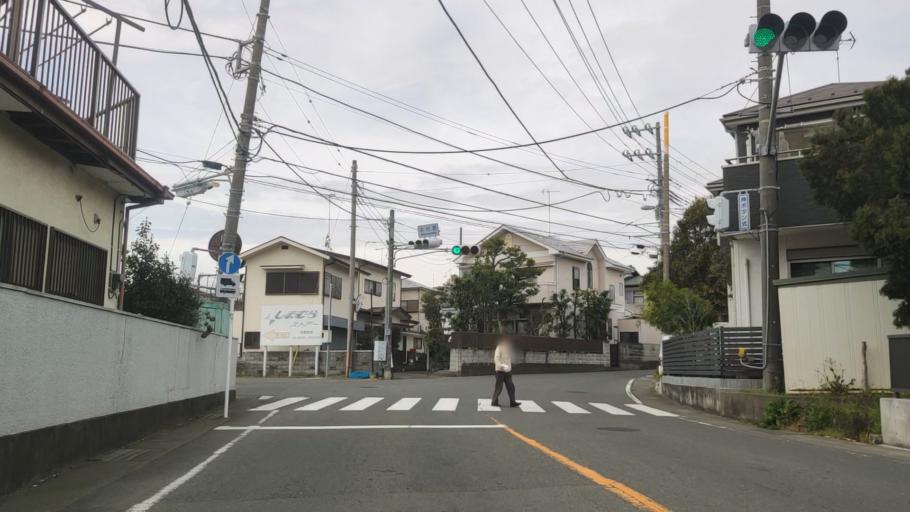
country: JP
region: Kanagawa
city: Ninomiya
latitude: 35.2916
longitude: 139.2350
